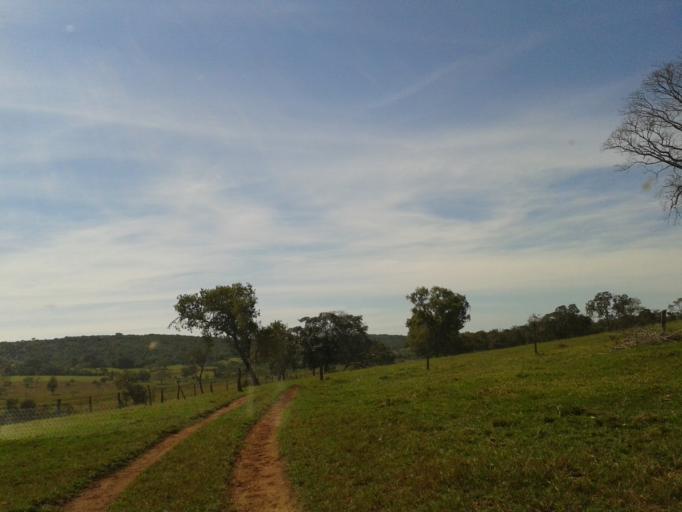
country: BR
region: Minas Gerais
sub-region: Campina Verde
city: Campina Verde
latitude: -19.4348
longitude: -49.6911
